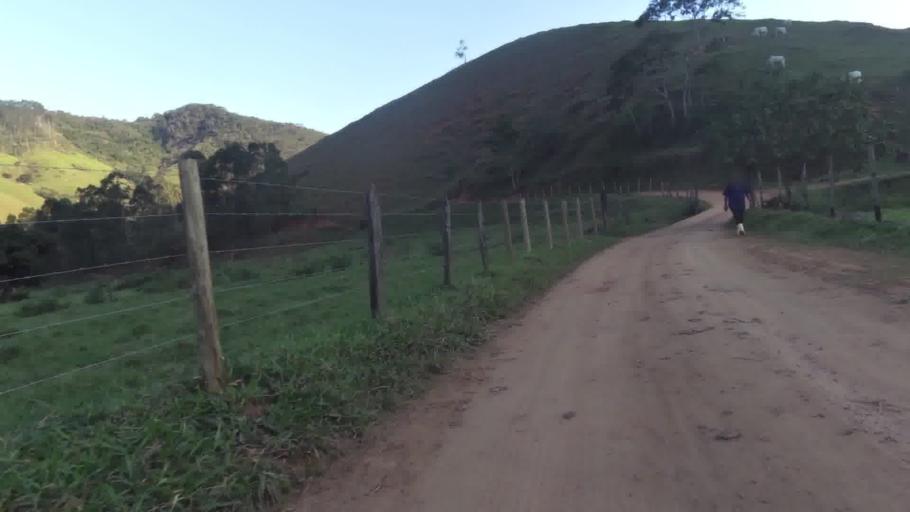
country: BR
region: Espirito Santo
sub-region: Alfredo Chaves
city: Alfredo Chaves
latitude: -20.6085
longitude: -40.7213
